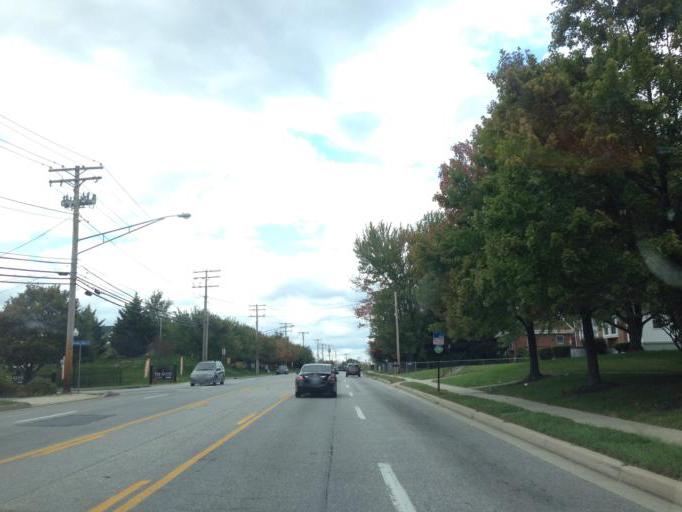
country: US
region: Maryland
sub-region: Baltimore County
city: Milford Mill
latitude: 39.3231
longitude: -76.7590
